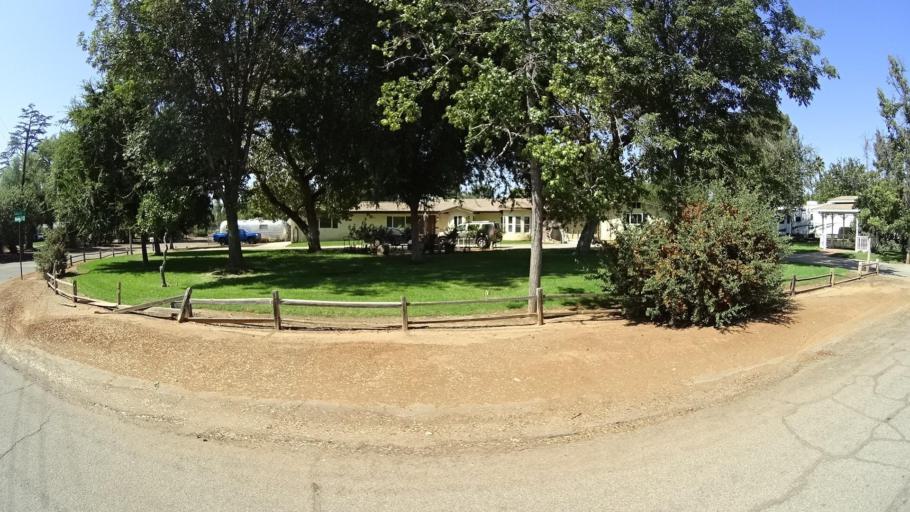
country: US
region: California
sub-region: San Diego County
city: Granite Hills
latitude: 32.8017
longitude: -116.9149
